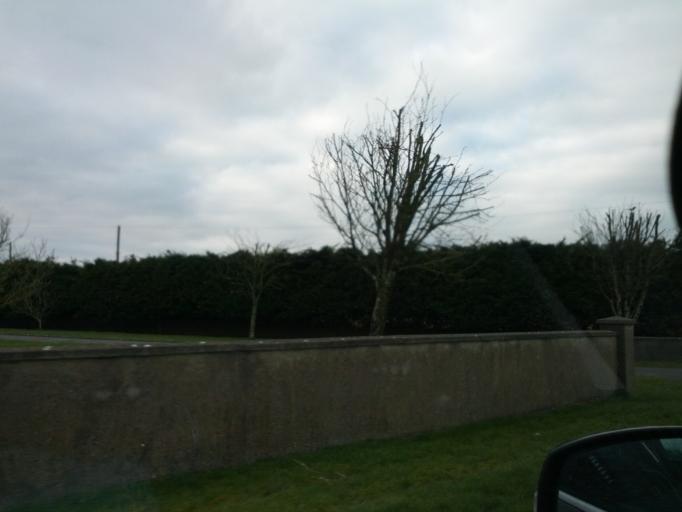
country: IE
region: Connaught
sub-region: County Galway
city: Gort
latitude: 53.1707
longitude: -8.8500
